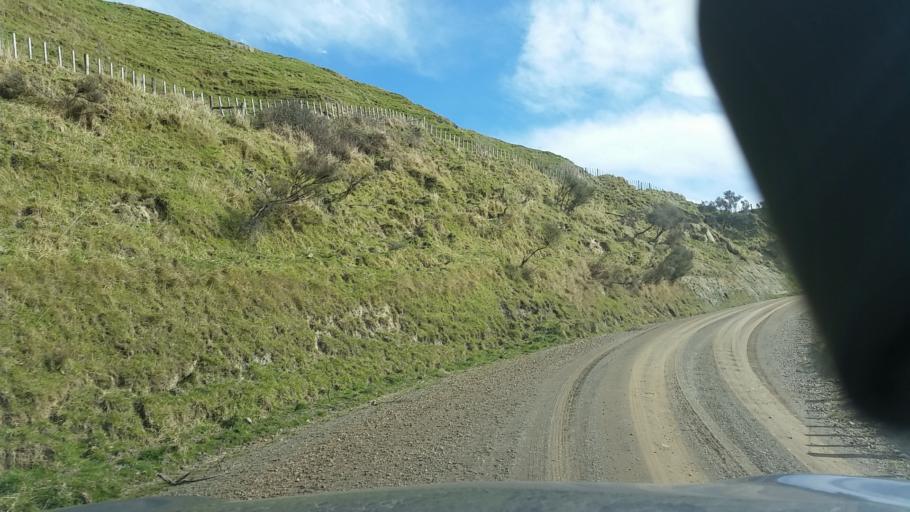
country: NZ
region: Hawke's Bay
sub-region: Napier City
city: Napier
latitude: -39.2109
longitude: 176.9648
